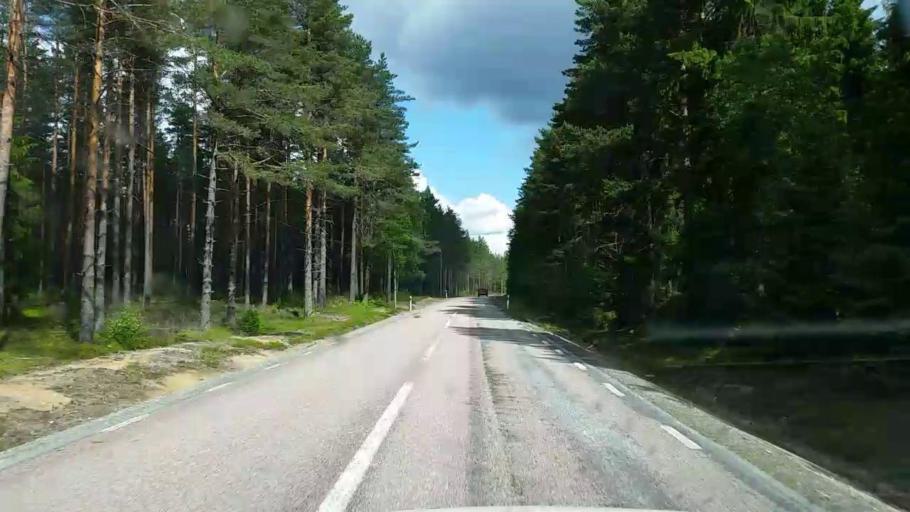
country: SE
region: Vaestmanland
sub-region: Skinnskattebergs Kommun
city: Skinnskatteberg
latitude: 59.8118
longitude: 15.8404
